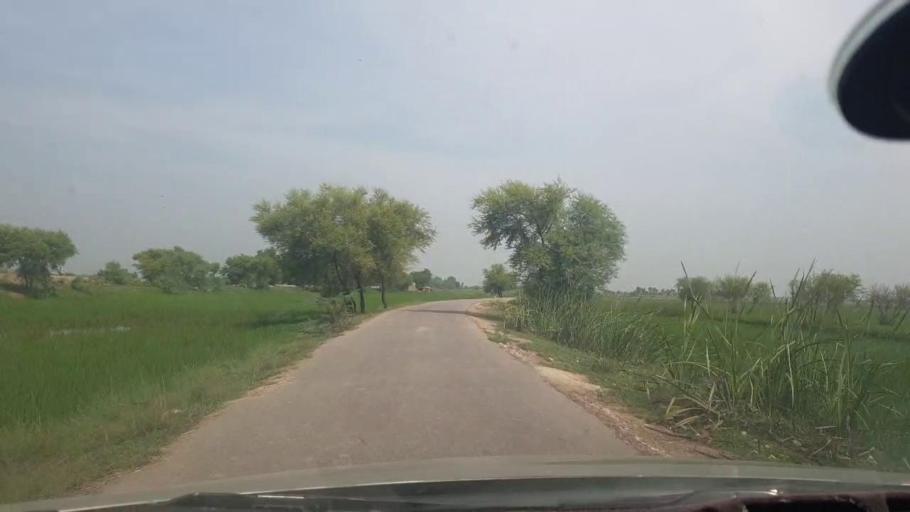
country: PK
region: Sindh
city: Jacobabad
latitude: 28.3017
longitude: 68.4751
